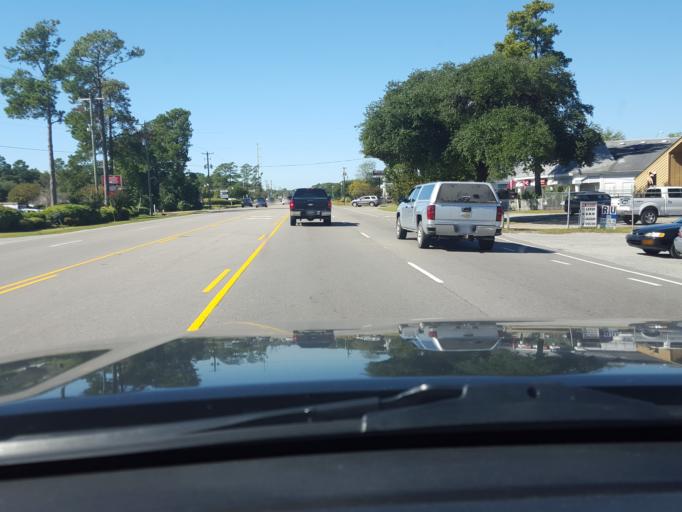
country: US
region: North Carolina
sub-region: New Hanover County
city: Seagate
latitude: 34.2091
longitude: -77.8479
